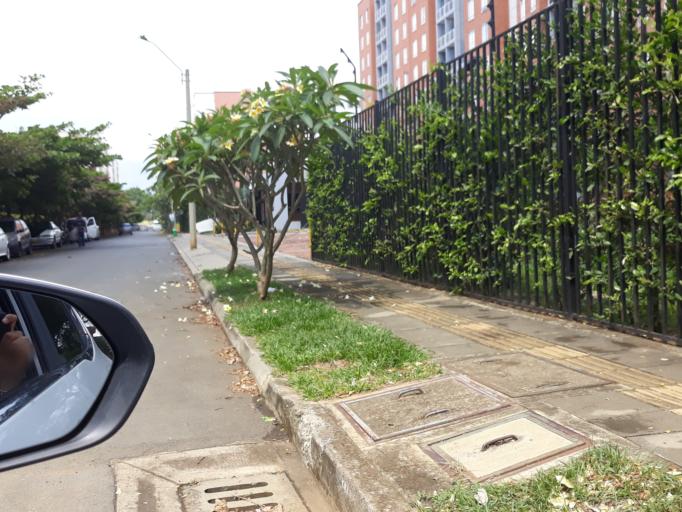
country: CO
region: Valle del Cauca
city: Cali
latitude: 3.3709
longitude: -76.5092
